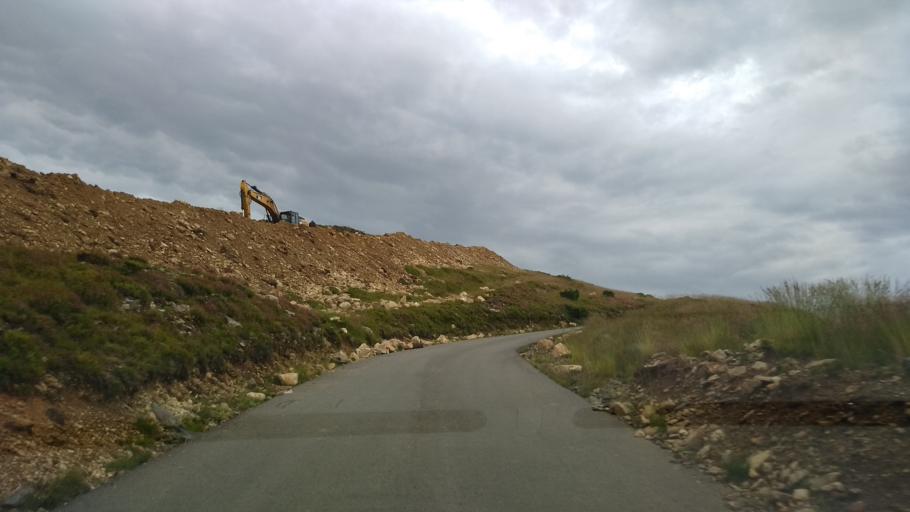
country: RO
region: Hunedoara
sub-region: Municipiul  Vulcan
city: Jiu-Paroseni
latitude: 45.3066
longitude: 23.3121
